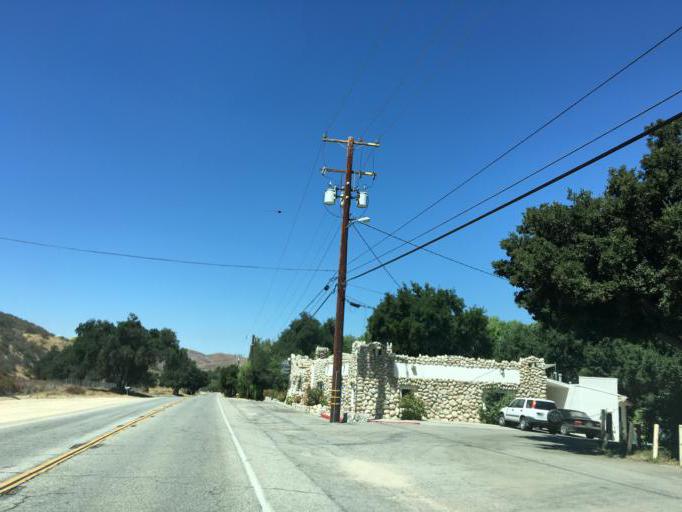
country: US
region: California
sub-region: Los Angeles County
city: Agua Dulce
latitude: 34.5108
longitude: -118.3552
